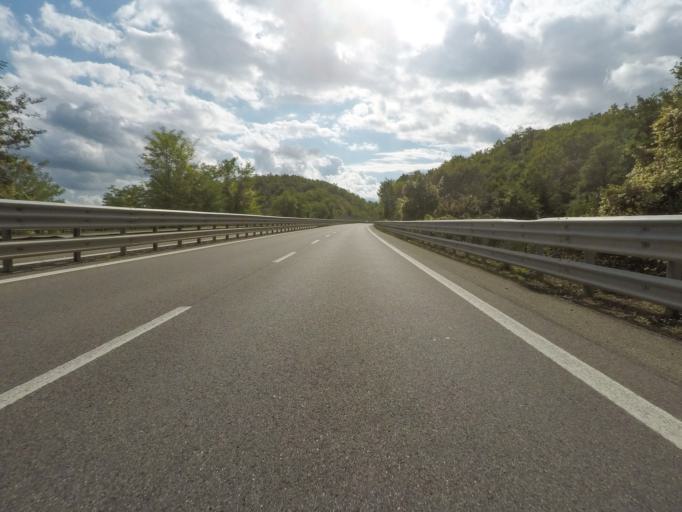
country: IT
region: Tuscany
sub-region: Provincia di Siena
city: Rapolano Terme
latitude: 43.2835
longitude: 11.6269
